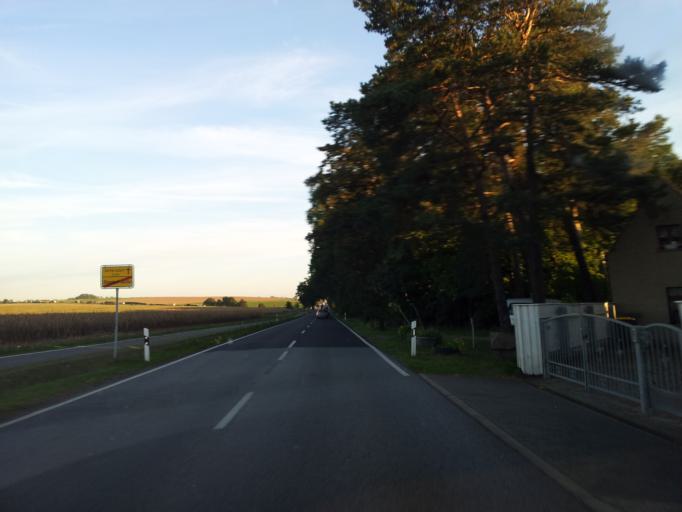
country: DE
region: Saxony
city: Ottendorf-Okrilla
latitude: 51.1787
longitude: 13.8504
